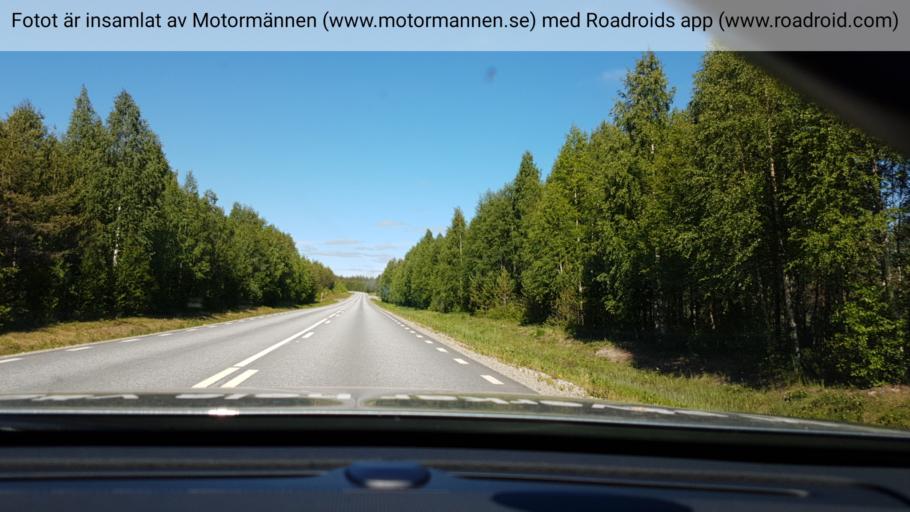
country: SE
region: Vaesterbotten
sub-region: Asele Kommun
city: Insjon
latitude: 64.1956
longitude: 17.6738
